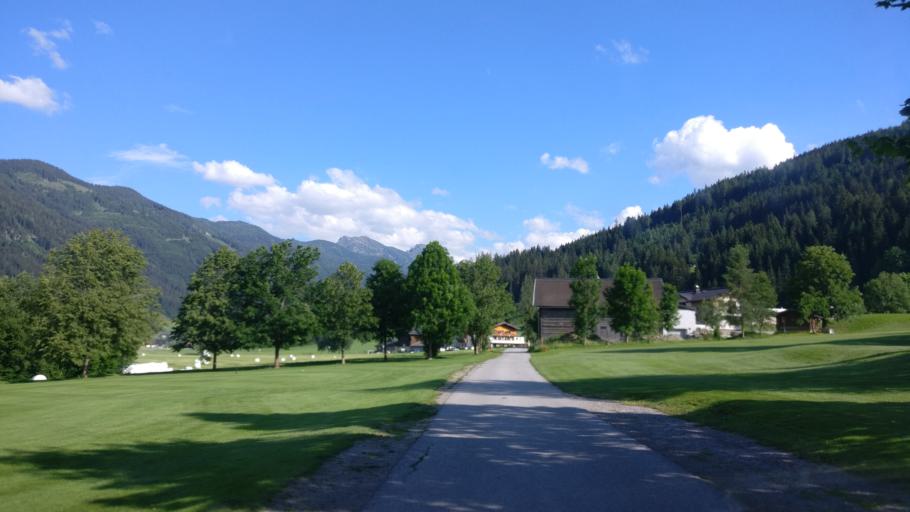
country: AT
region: Salzburg
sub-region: Politischer Bezirk Sankt Johann im Pongau
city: Radstadt
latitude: 47.3713
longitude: 13.4765
